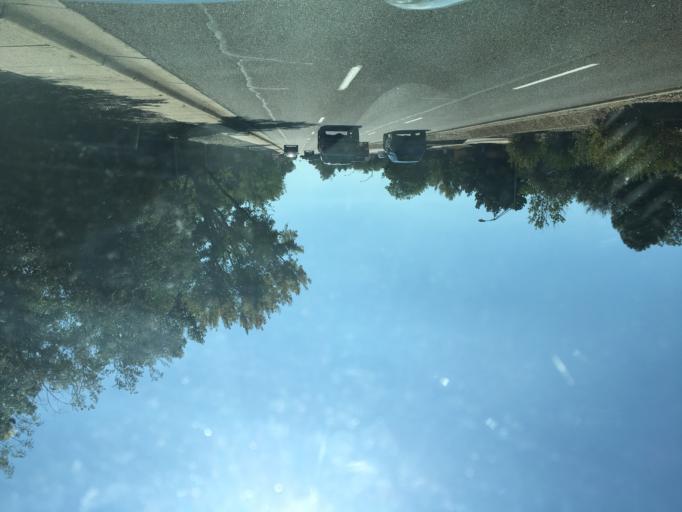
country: US
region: Colorado
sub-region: Arapahoe County
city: Dove Valley
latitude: 39.6310
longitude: -104.8058
